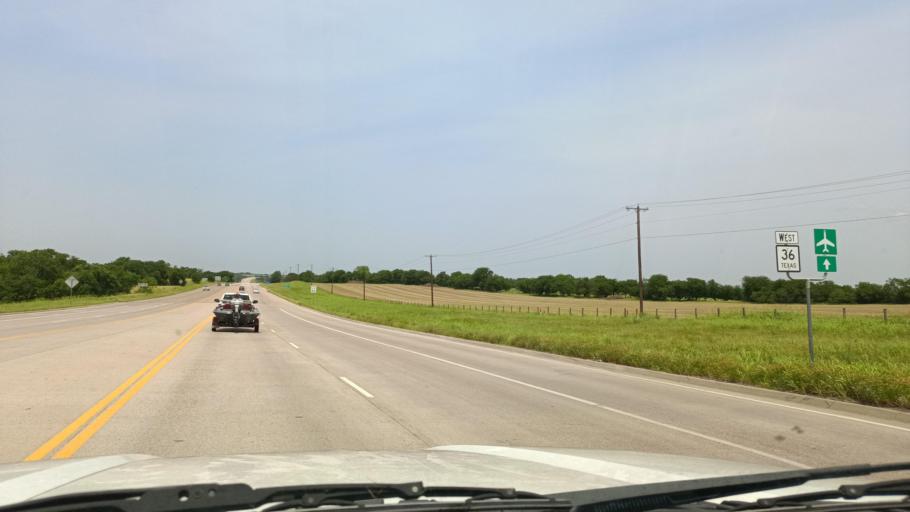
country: US
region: Texas
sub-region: Bell County
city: Temple
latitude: 31.1199
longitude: -97.3858
